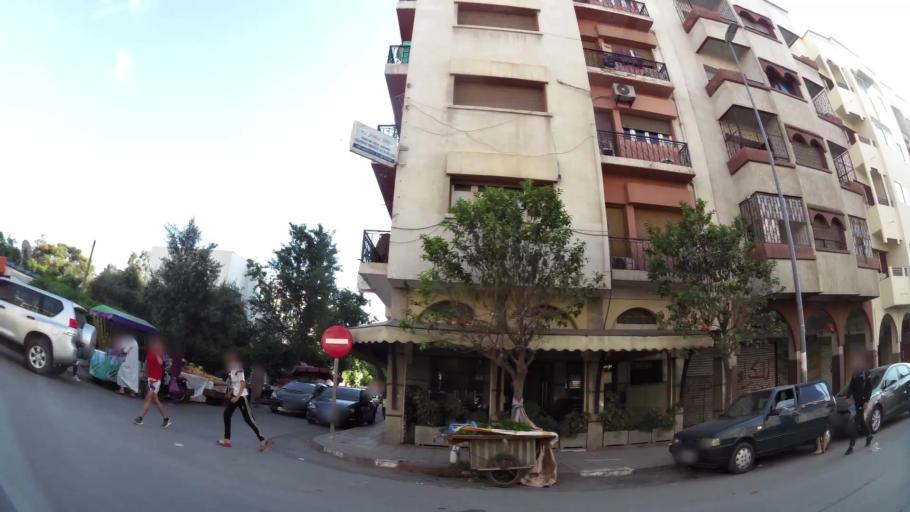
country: MA
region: Rabat-Sale-Zemmour-Zaer
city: Sale
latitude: 34.0542
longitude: -6.7933
